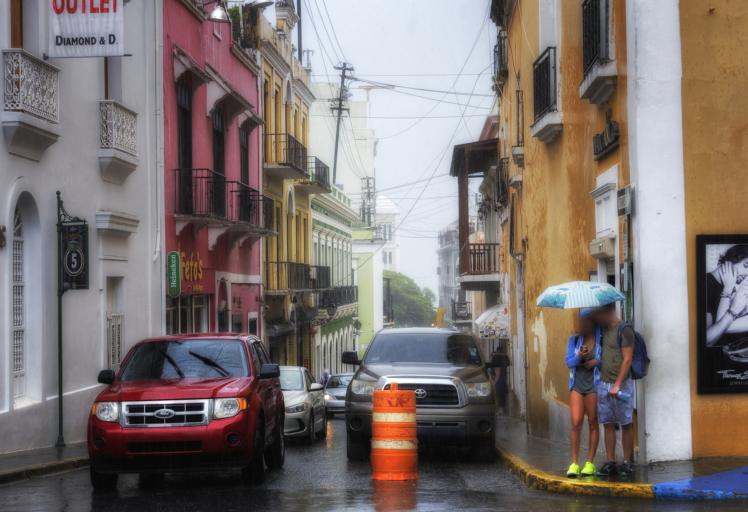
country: PR
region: San Juan
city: San Juan
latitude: 18.4662
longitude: -66.1144
